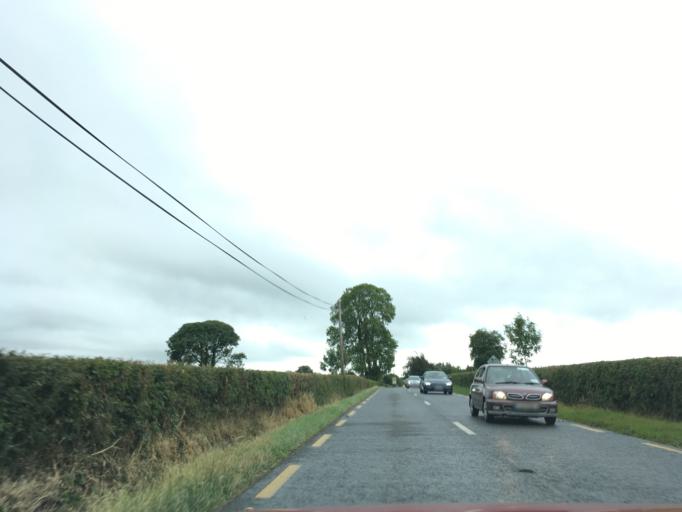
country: IE
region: Munster
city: Fethard
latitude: 52.4261
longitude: -7.7747
